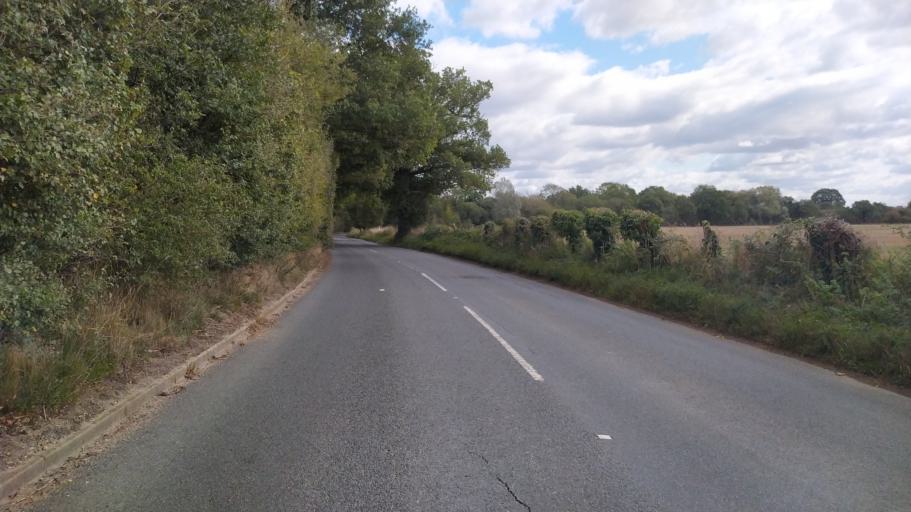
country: GB
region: England
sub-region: Wokingham
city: Shinfield
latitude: 51.4136
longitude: -0.9856
